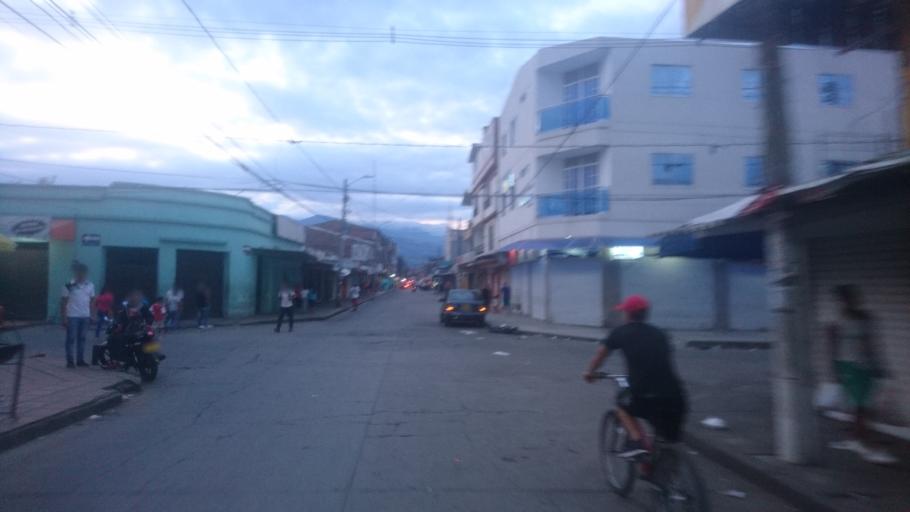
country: CO
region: Valle del Cauca
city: Jamundi
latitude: 3.2604
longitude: -76.5388
